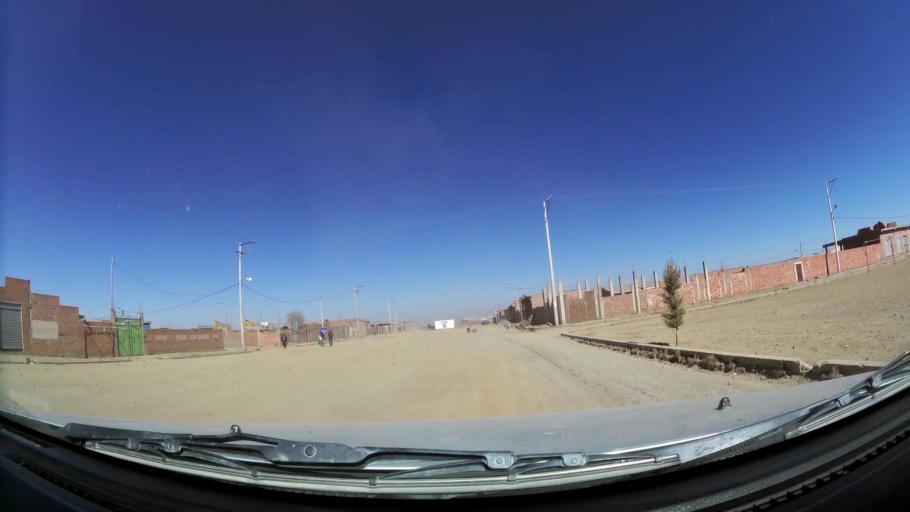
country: BO
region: La Paz
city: La Paz
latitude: -16.6250
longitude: -68.1928
